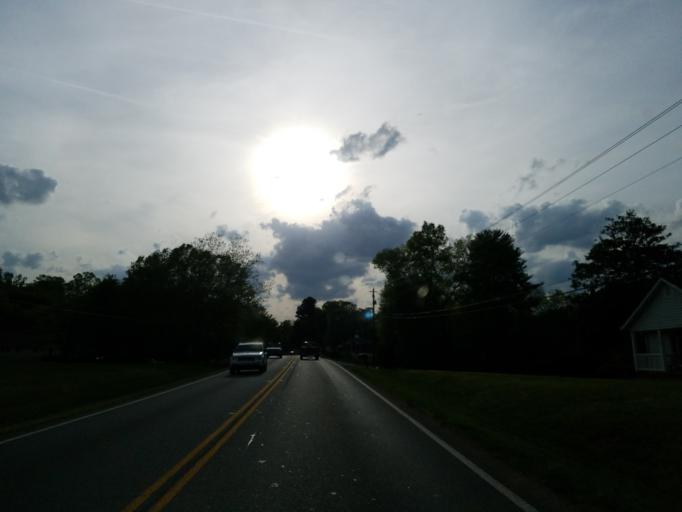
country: US
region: Georgia
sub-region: Cherokee County
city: Canton
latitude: 34.2413
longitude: -84.4190
